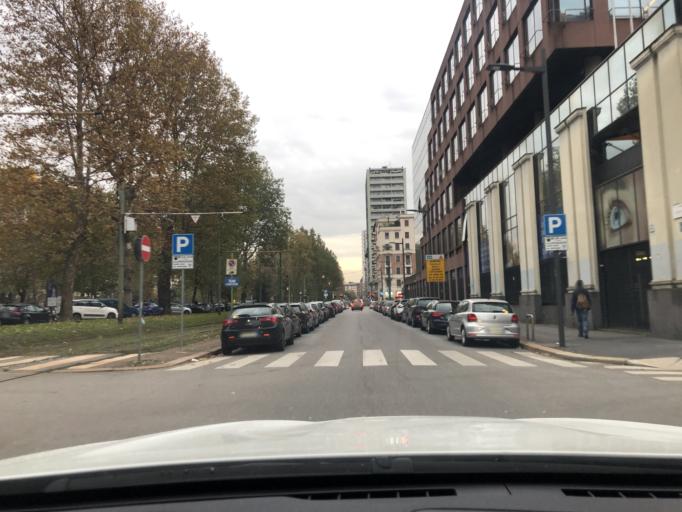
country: IT
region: Lombardy
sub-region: Citta metropolitana di Milano
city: Milano
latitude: 45.4832
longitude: 9.1619
